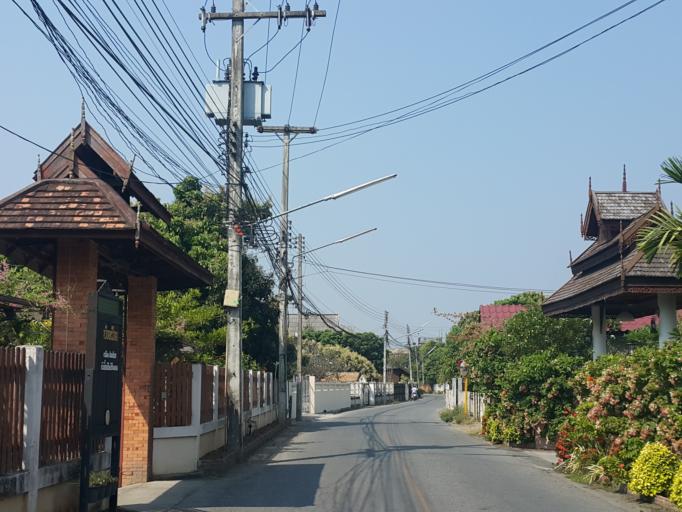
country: TH
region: Chiang Mai
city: San Kamphaeng
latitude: 18.7427
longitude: 99.1317
